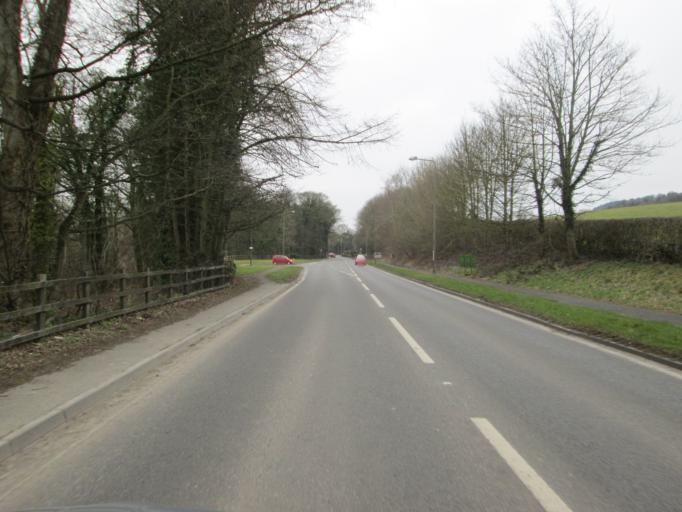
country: GB
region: England
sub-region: Derbyshire
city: Matlock
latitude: 53.1791
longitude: -1.6099
